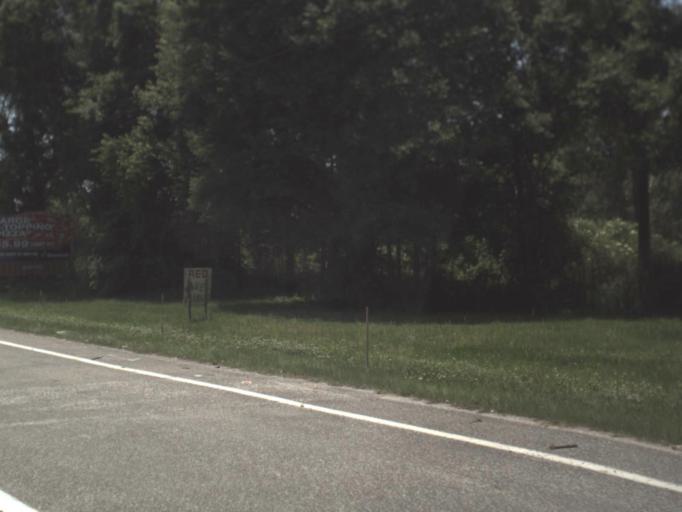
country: US
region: Florida
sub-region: Bradford County
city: Starke
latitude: 30.0352
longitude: -82.0756
